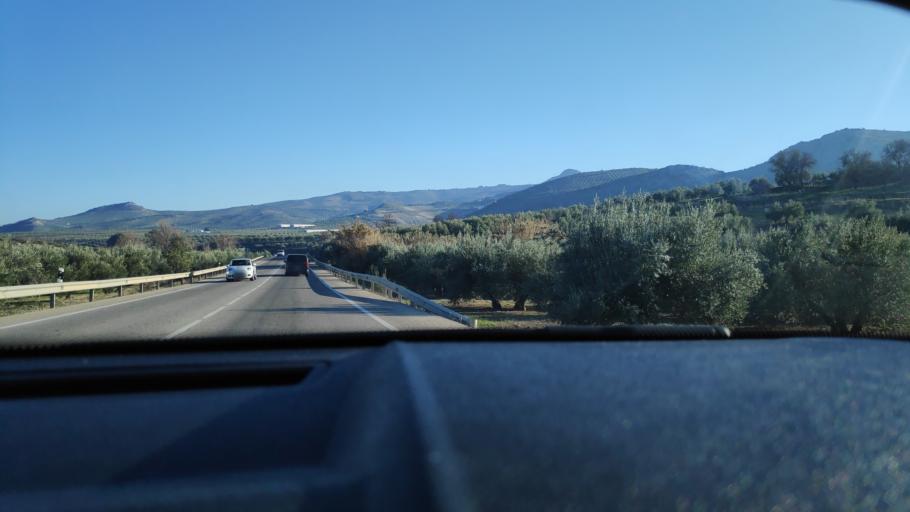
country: ES
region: Andalusia
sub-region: Province of Cordoba
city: Luque
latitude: 37.5701
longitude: -4.2512
